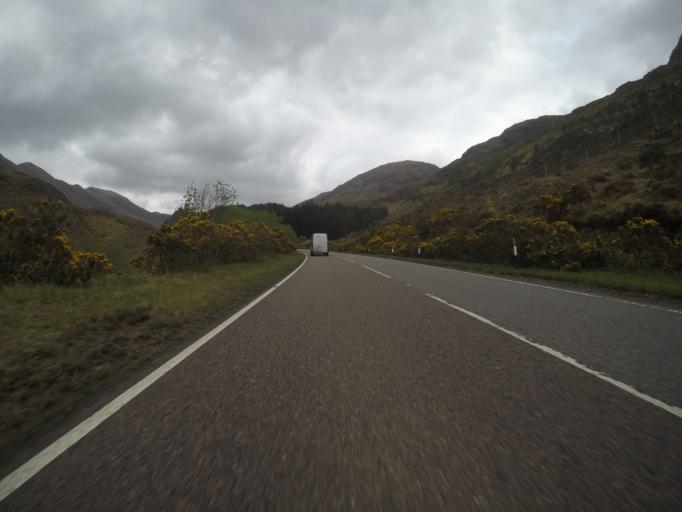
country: GB
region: Scotland
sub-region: Highland
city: Fort William
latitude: 57.1644
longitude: -5.3305
